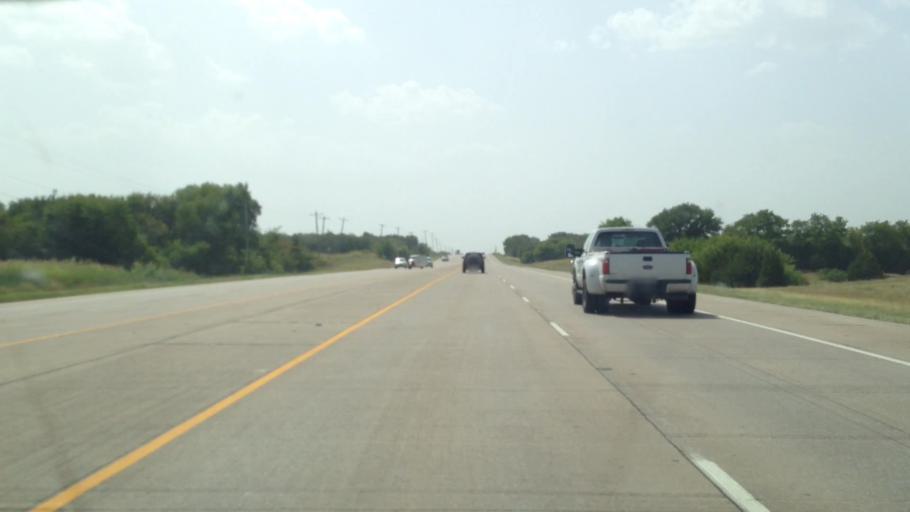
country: US
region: Texas
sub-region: Collin County
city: Princeton
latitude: 33.1701
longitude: -96.4730
